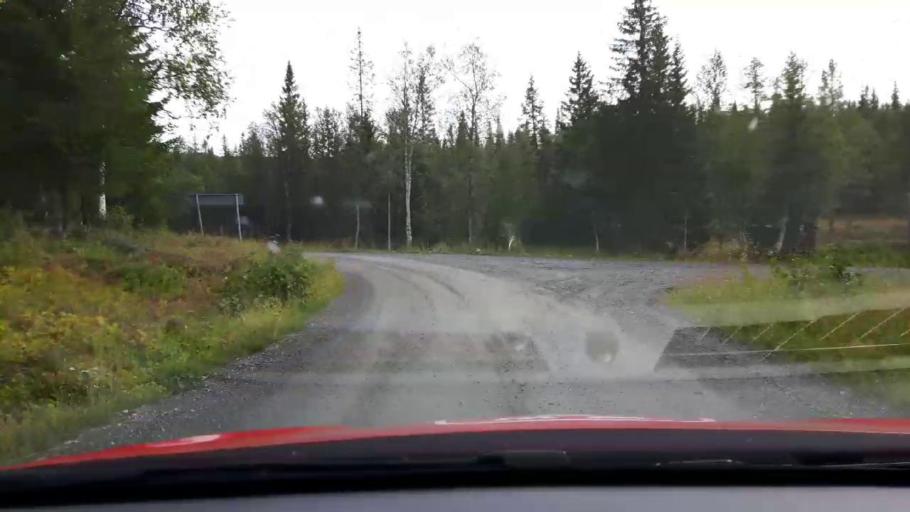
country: SE
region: Jaemtland
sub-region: Are Kommun
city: Are
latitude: 63.7742
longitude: 13.0707
